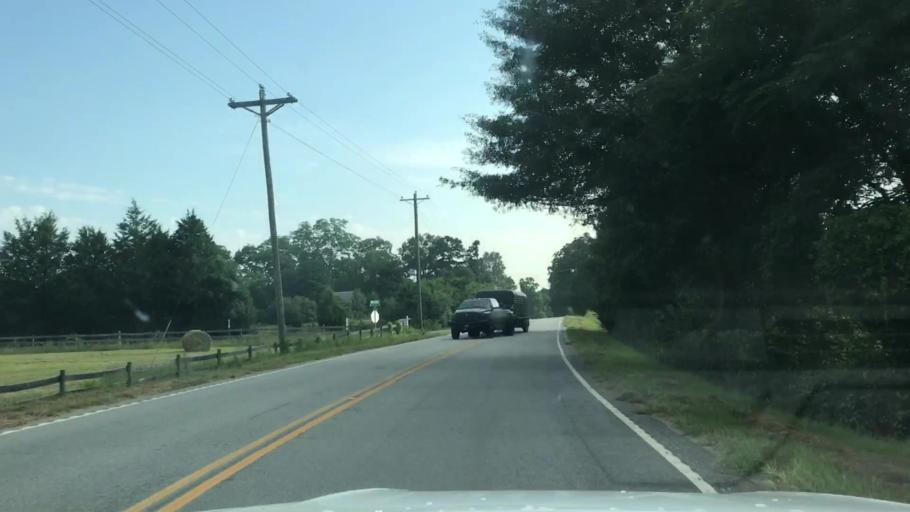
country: US
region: South Carolina
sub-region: Spartanburg County
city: Roebuck
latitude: 34.8184
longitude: -81.9266
